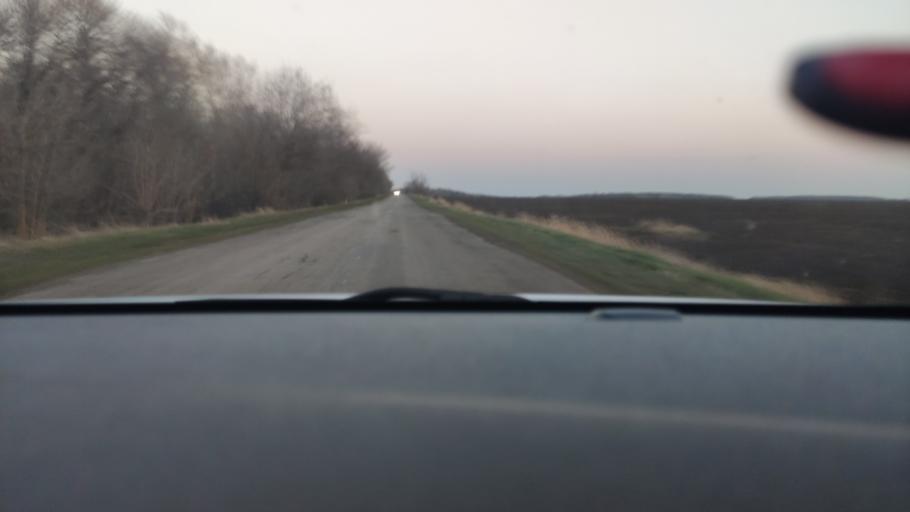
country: RU
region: Voronezj
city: Uryv-Pokrovka
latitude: 51.1228
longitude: 39.1249
